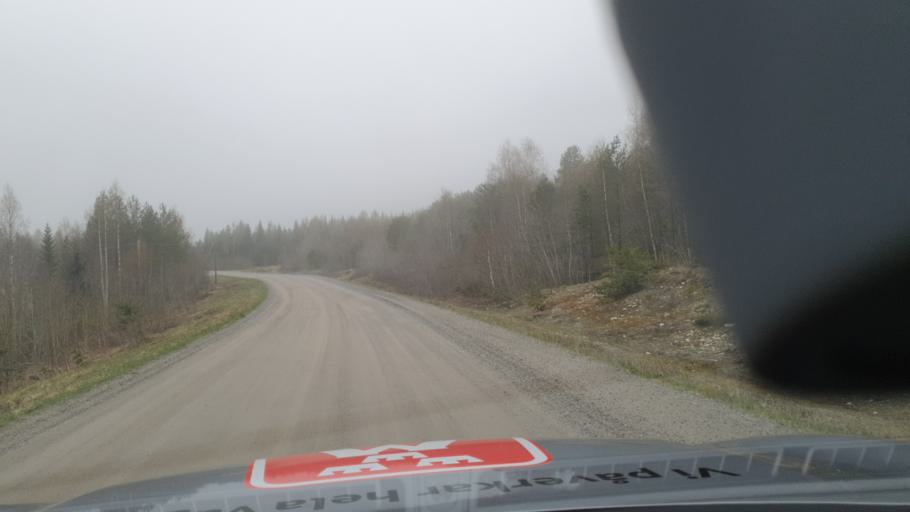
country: SE
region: Vaesternorrland
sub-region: OErnskoeldsviks Kommun
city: Husum
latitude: 63.6120
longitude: 19.0260
